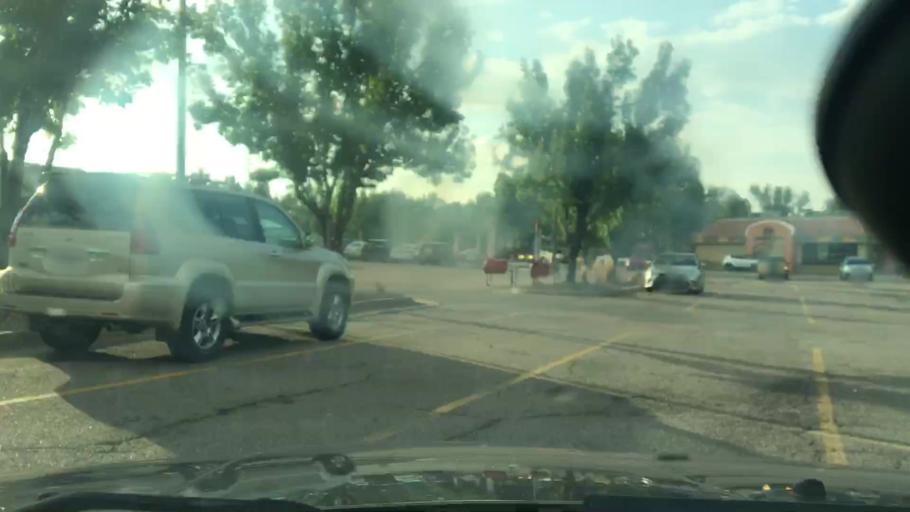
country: US
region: Colorado
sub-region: Arapahoe County
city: Glendale
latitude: 39.6665
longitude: -104.9134
